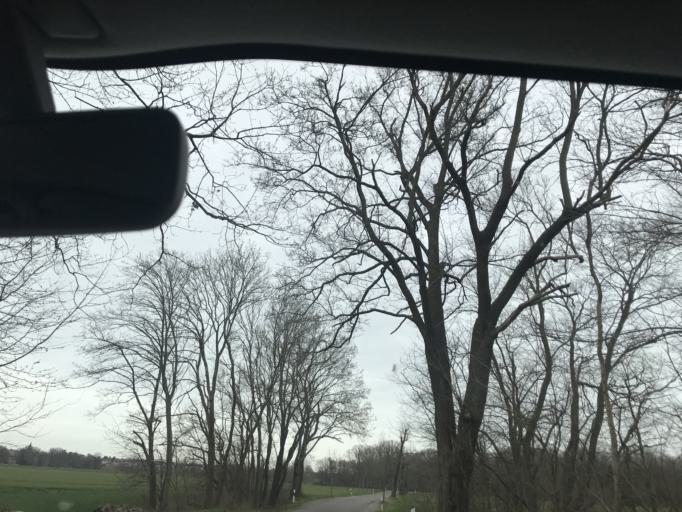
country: DE
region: Saxony
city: Schkeuditz
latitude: 51.3750
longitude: 12.2617
